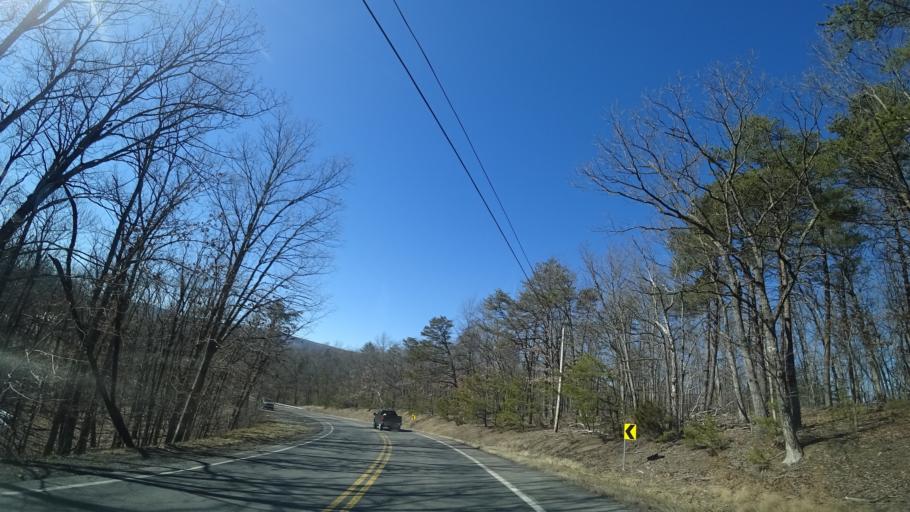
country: US
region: Virginia
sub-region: Shenandoah County
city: Strasburg
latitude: 39.0755
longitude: -78.4121
